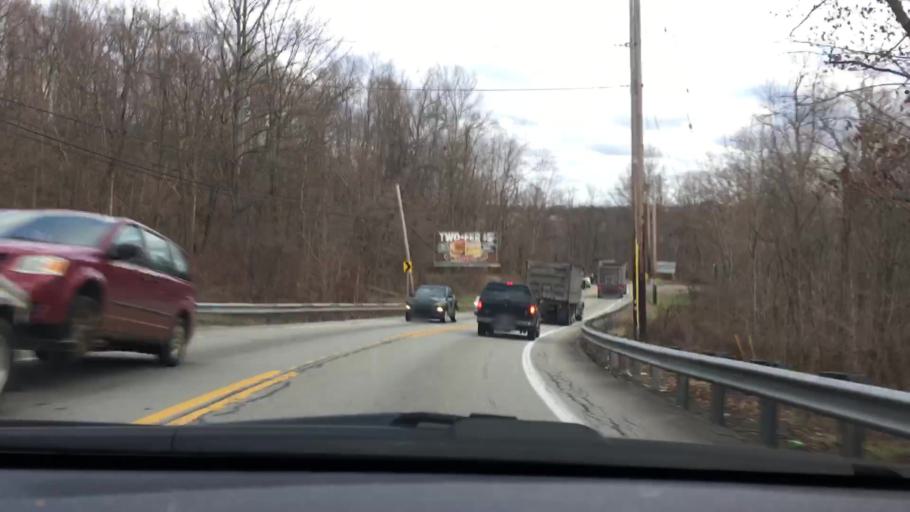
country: US
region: Pennsylvania
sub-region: Westmoreland County
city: Trafford
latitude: 40.3866
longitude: -79.7745
